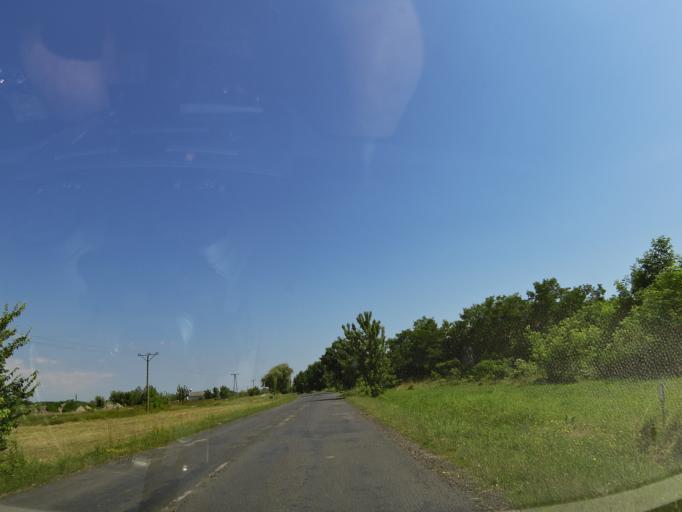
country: HU
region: Jasz-Nagykun-Szolnok
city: Abadszalok
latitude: 47.4669
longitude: 20.5926
